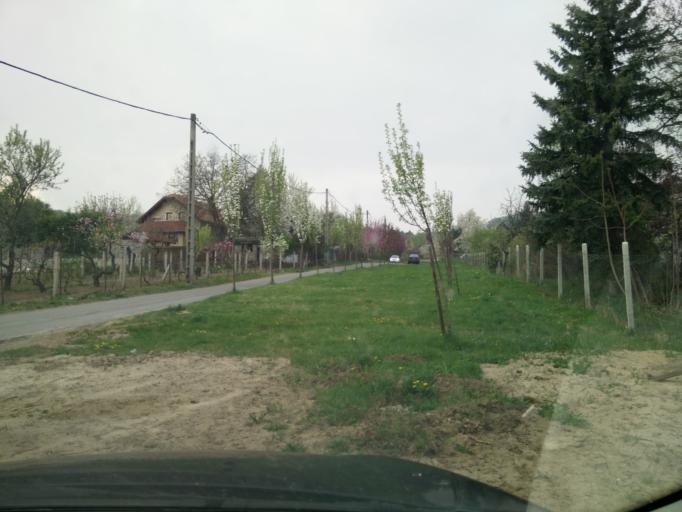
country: HU
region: Pest
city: Budaors
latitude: 47.4684
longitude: 18.9395
